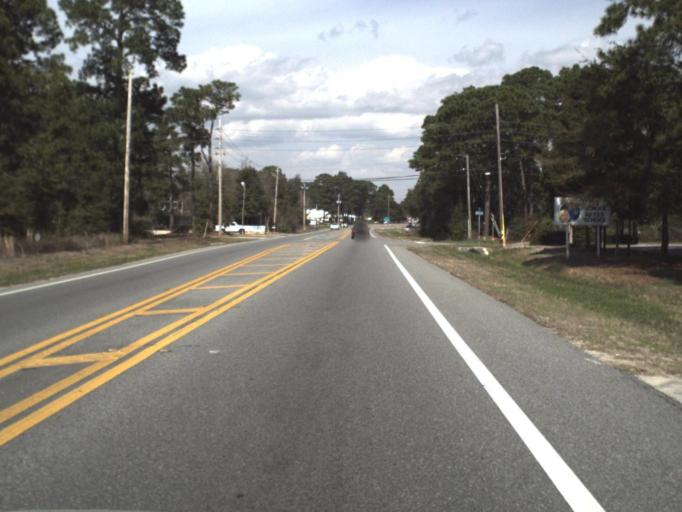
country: US
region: Florida
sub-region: Bay County
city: Pretty Bayou
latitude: 30.2105
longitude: -85.6718
